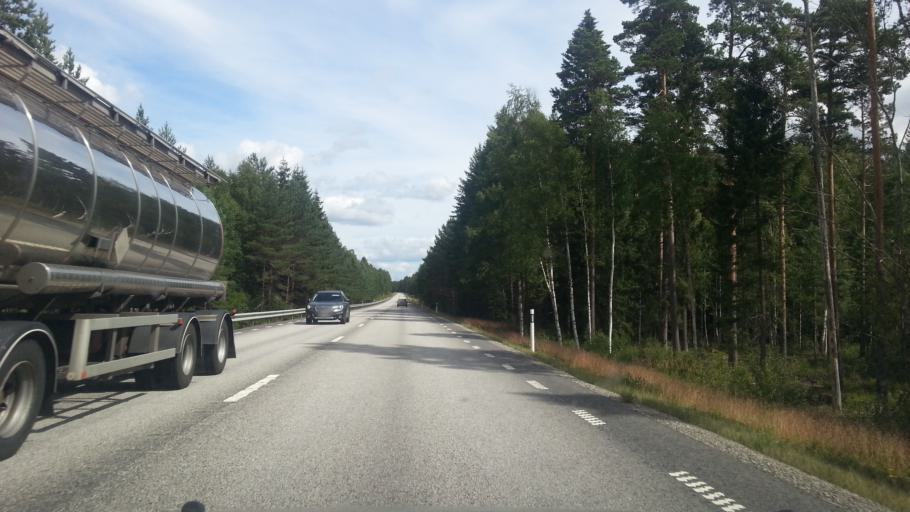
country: SE
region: OErebro
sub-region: Lindesbergs Kommun
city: Lindesberg
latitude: 59.6745
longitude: 15.2983
